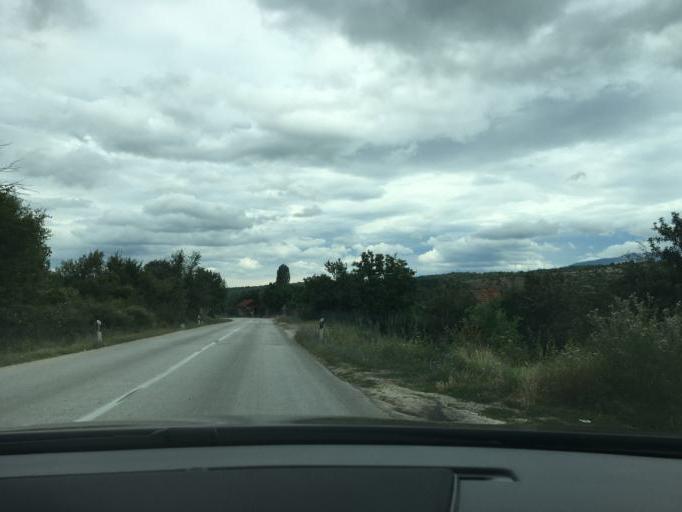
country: MK
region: Kriva Palanka
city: Kriva Palanka
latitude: 42.1789
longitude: 22.2697
